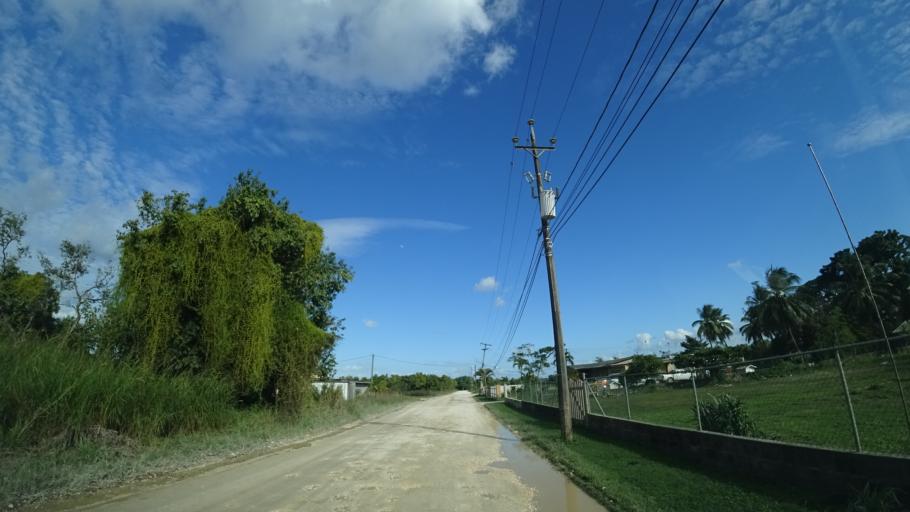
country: BZ
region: Belize
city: Belize City
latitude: 17.5566
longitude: -88.4027
